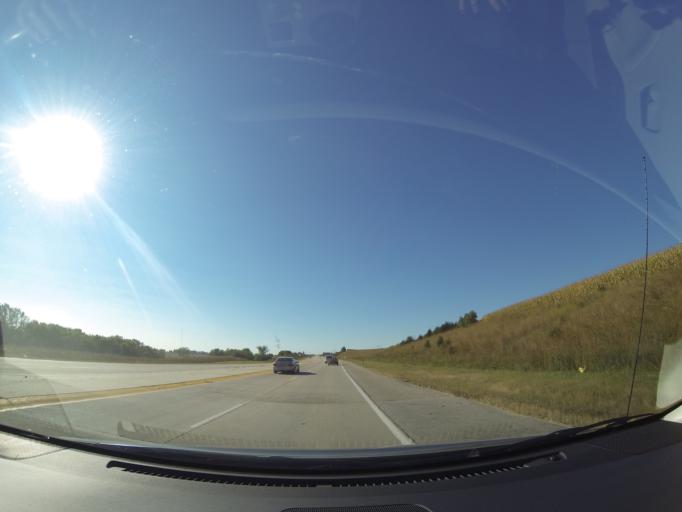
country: US
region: Nebraska
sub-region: Sarpy County
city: Gretna
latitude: 41.1155
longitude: -96.2533
